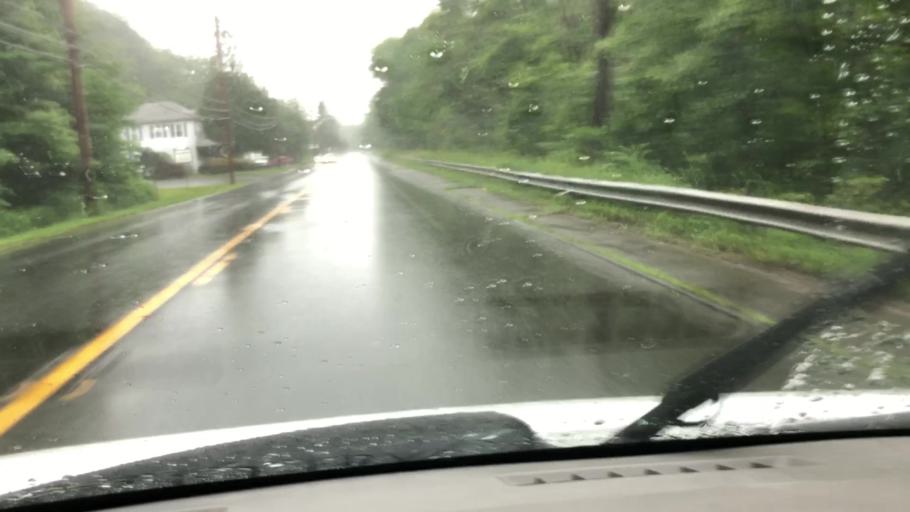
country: US
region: Massachusetts
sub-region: Berkshire County
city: Adams
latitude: 42.6028
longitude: -73.1371
